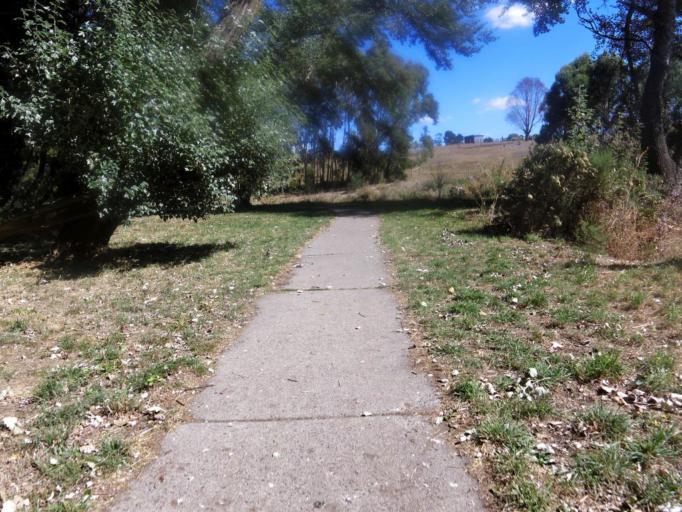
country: AU
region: Victoria
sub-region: Mount Alexander
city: Castlemaine
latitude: -37.2514
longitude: 144.4451
